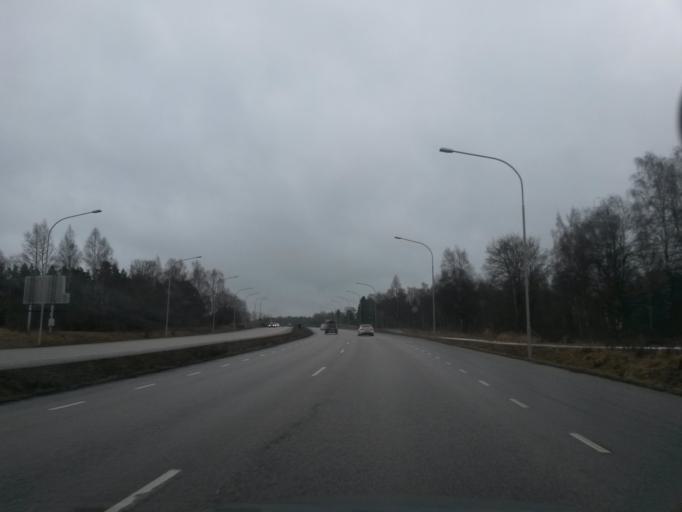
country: SE
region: Vaestra Goetaland
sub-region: Vanersborgs Kommun
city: Vanersborg
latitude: 58.3598
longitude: 12.3121
